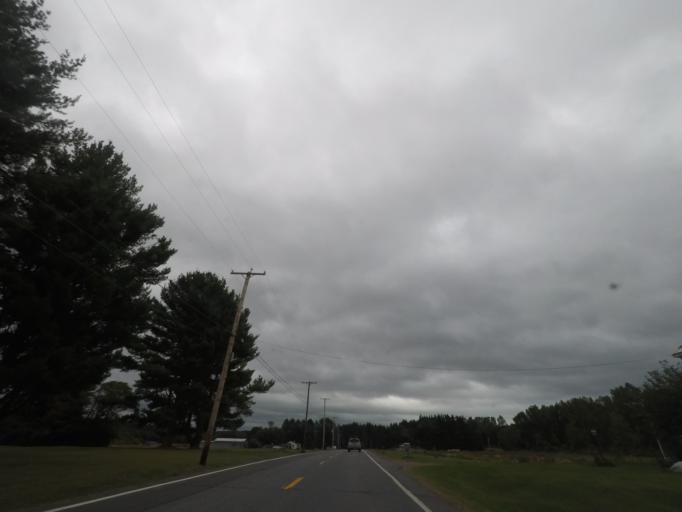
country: US
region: New York
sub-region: Washington County
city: Cambridge
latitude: 42.9526
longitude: -73.4239
